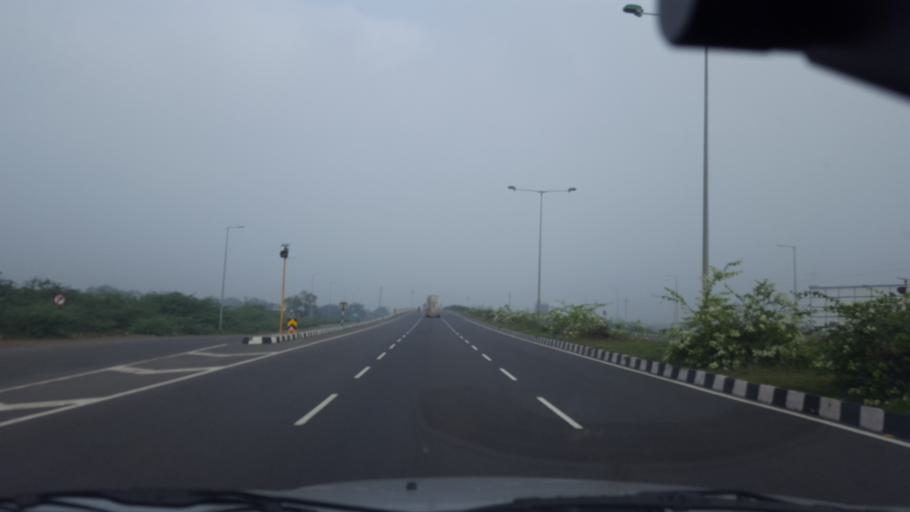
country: IN
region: Andhra Pradesh
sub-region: Prakasam
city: Ongole
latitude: 15.5300
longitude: 80.0550
